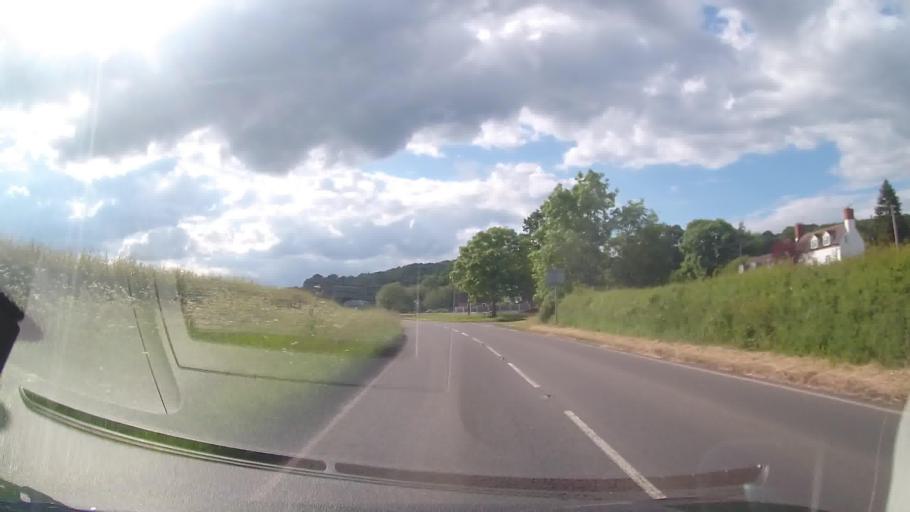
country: GB
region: England
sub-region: Shropshire
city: Much Wenlock
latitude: 52.6396
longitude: -2.5391
